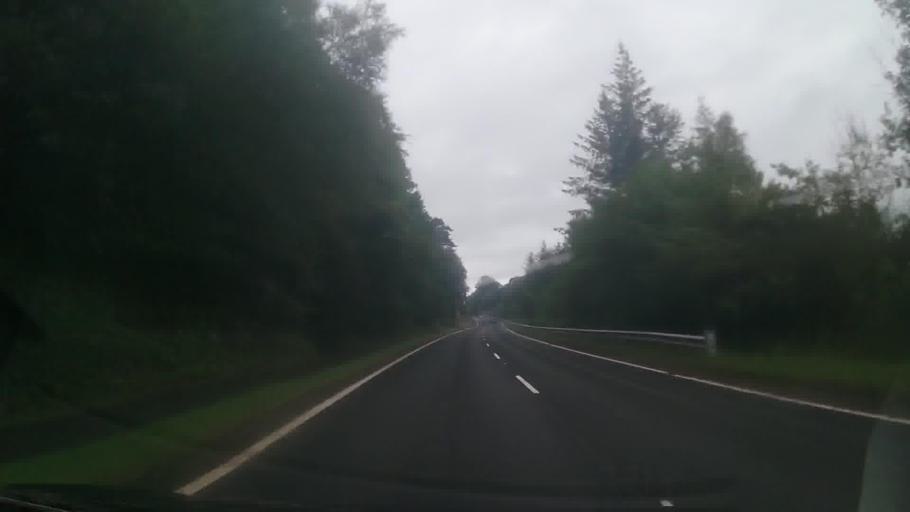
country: GB
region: Scotland
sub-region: Highland
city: Fort William
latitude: 56.6830
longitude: -5.1656
